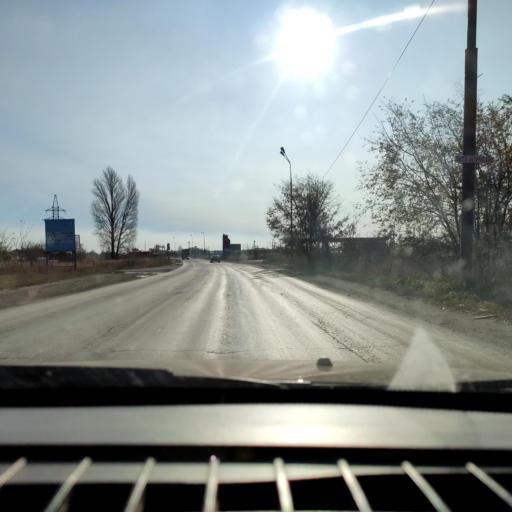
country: RU
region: Samara
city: Tol'yatti
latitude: 53.5734
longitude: 49.3405
